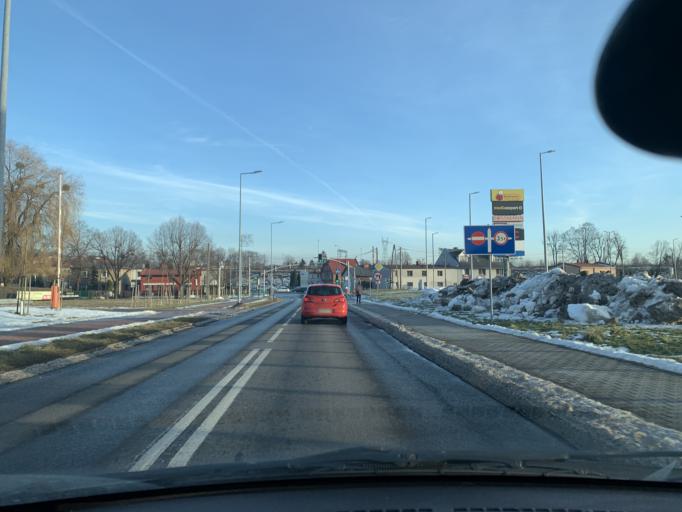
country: PL
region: Silesian Voivodeship
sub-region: Powiat tarnogorski
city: Radzionkow
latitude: 50.3967
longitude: 18.8960
